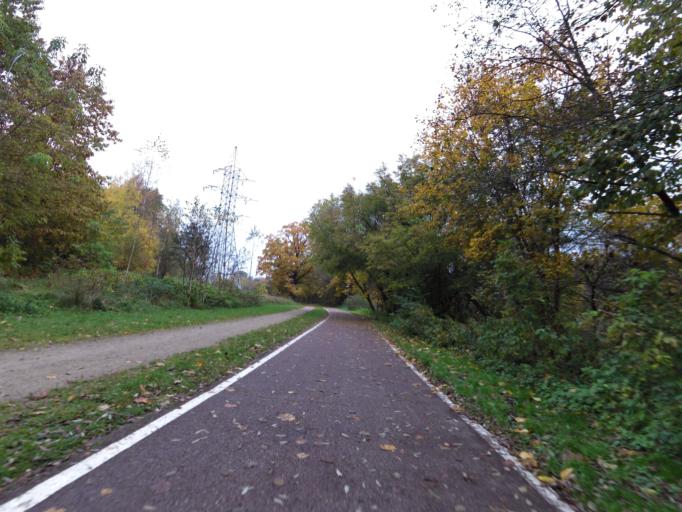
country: LT
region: Vilnius County
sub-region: Vilnius
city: Vilnius
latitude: 54.7270
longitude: 25.3093
